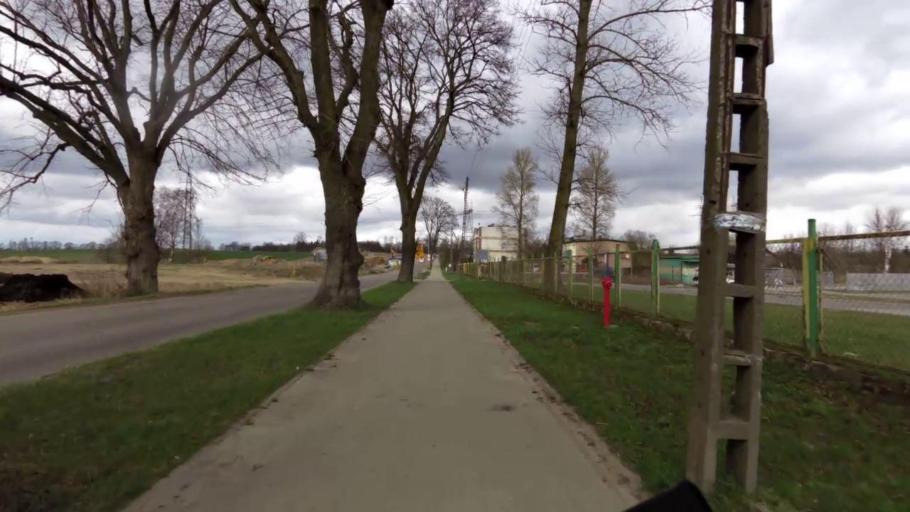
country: PL
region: West Pomeranian Voivodeship
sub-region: Powiat koszalinski
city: Sianow
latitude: 54.2369
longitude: 16.2986
